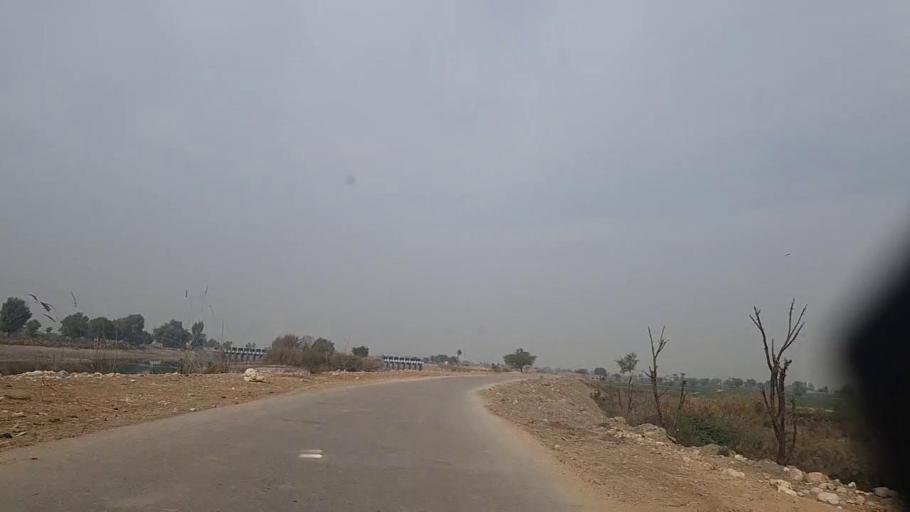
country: PK
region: Sindh
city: Sakrand
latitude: 26.2803
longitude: 68.2279
